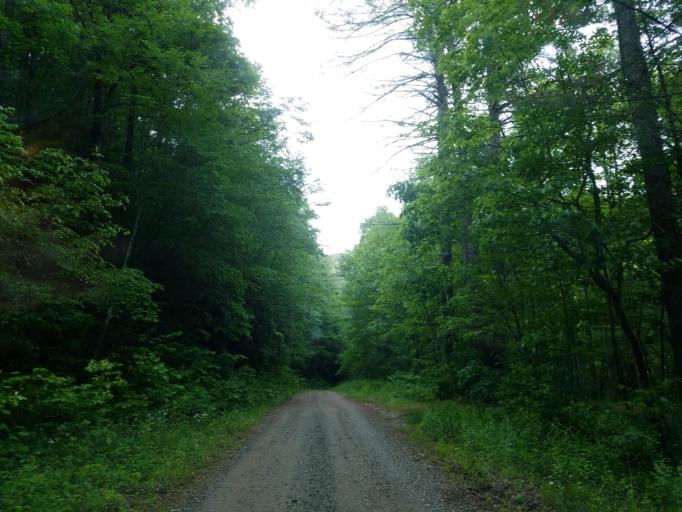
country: US
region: Georgia
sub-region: Union County
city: Blairsville
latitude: 34.7565
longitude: -84.0232
